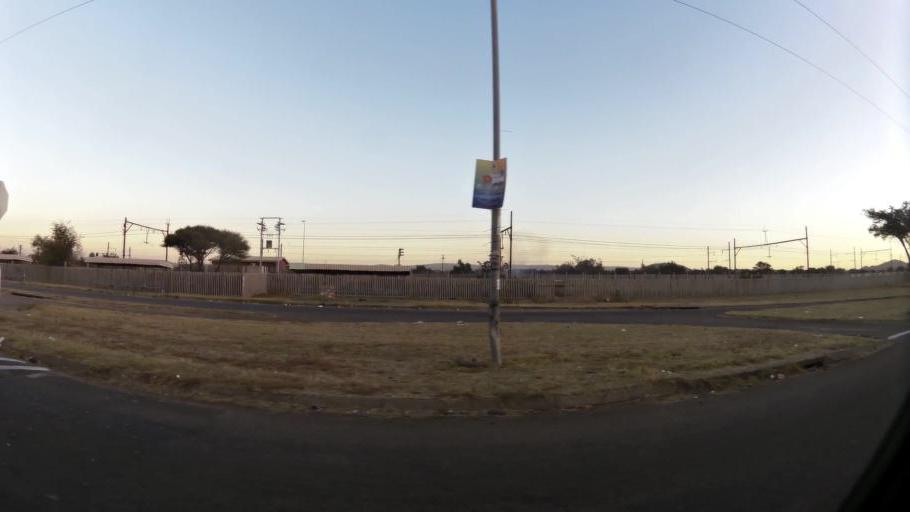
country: ZA
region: North-West
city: Ga-Rankuwa
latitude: -25.6212
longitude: 28.0170
